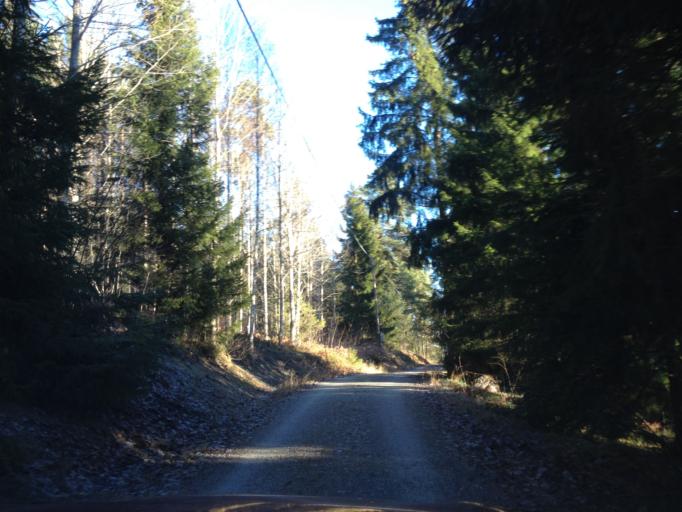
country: SE
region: Stockholm
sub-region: Sodertalje Kommun
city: Soedertaelje
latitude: 59.1634
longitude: 17.5794
